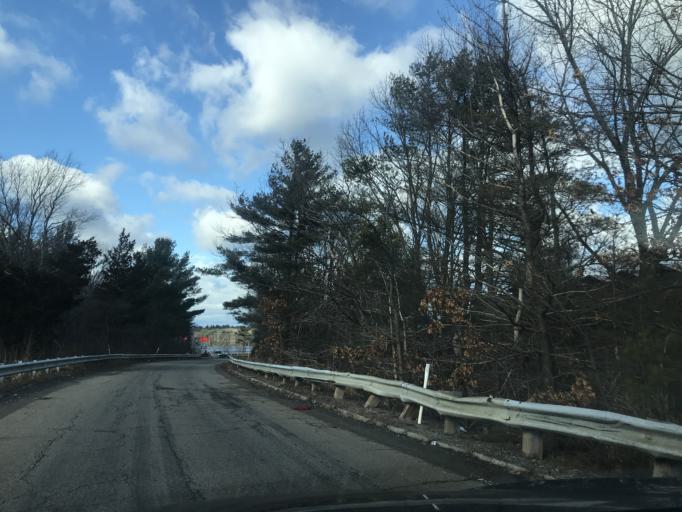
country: US
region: Massachusetts
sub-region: Plymouth County
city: Rockland
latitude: 42.1651
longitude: -70.8895
